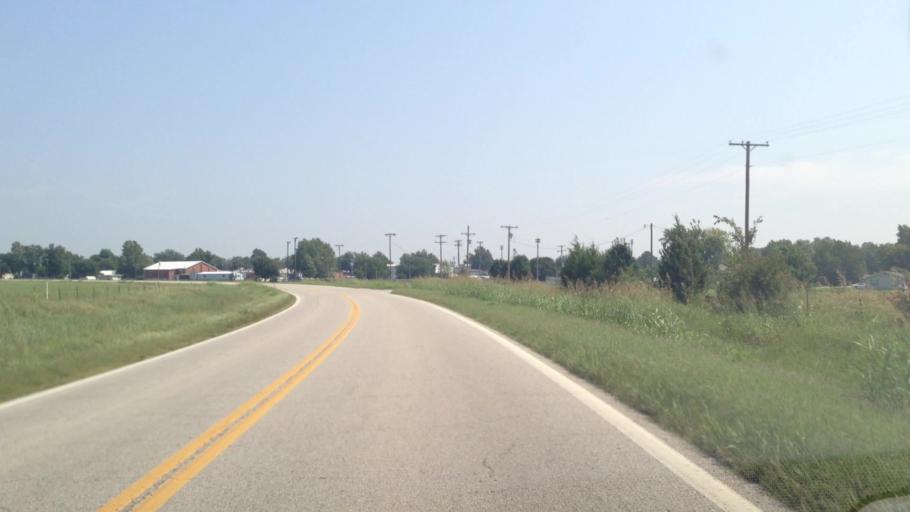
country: US
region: Kansas
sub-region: Labette County
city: Chetopa
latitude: 36.8676
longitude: -95.1021
